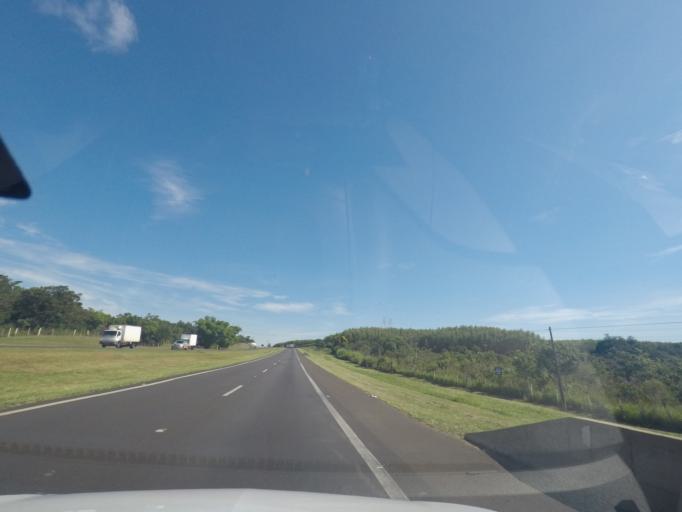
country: BR
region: Sao Paulo
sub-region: Itirapina
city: Itirapina
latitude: -22.1473
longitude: -47.7969
